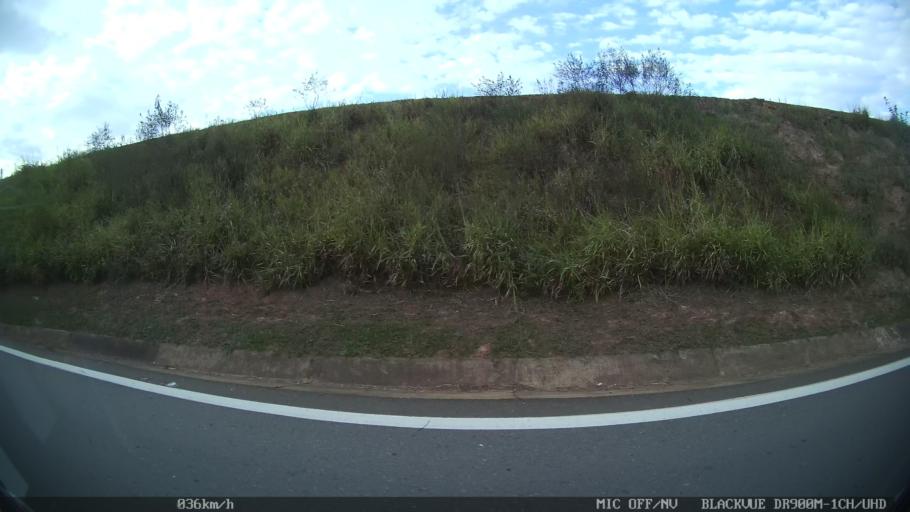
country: BR
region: Sao Paulo
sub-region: Americana
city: Americana
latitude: -22.6394
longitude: -47.3297
